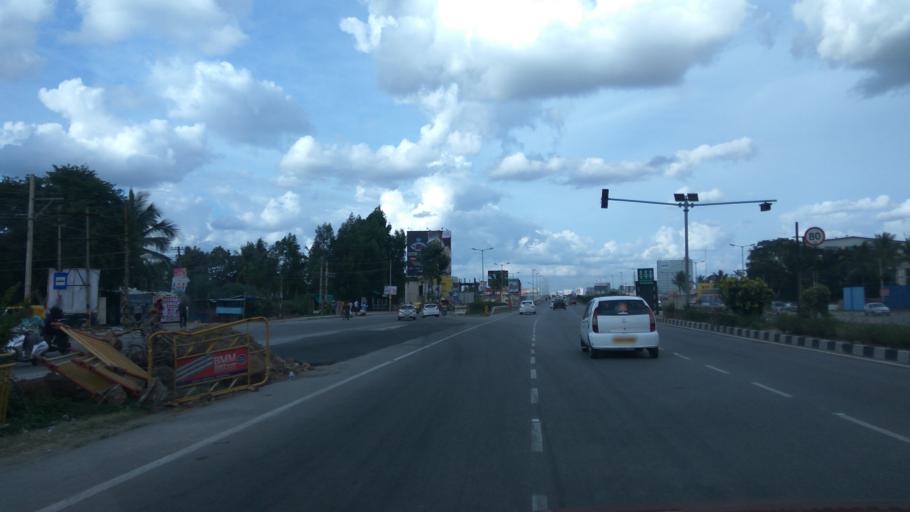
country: IN
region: Karnataka
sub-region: Bangalore Urban
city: Yelahanka
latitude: 13.1562
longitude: 77.6229
